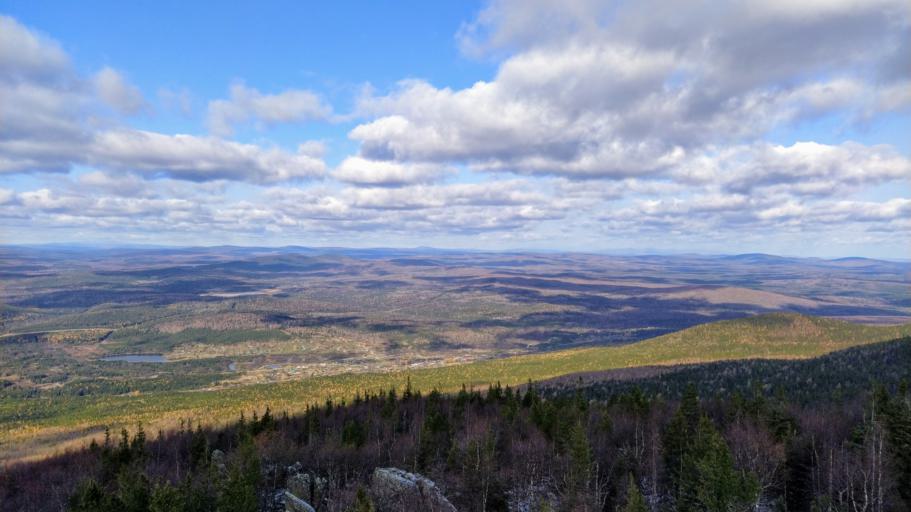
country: RU
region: Sverdlovsk
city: Kachkanar
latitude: 58.7708
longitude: 59.3761
